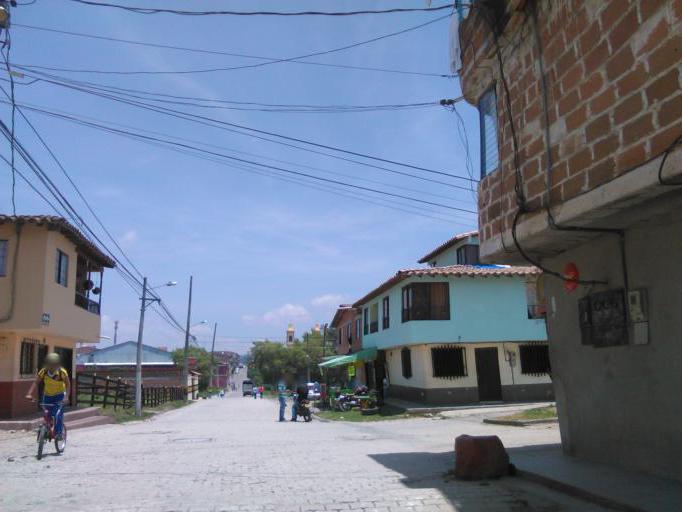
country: CO
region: Antioquia
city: La Union
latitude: 5.9700
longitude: -75.3604
